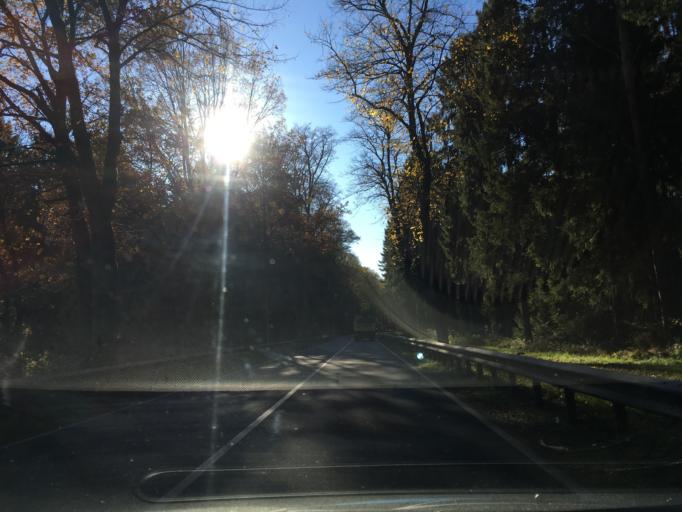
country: DE
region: Lower Saxony
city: Soderstorf
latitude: 53.1072
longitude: 10.1719
